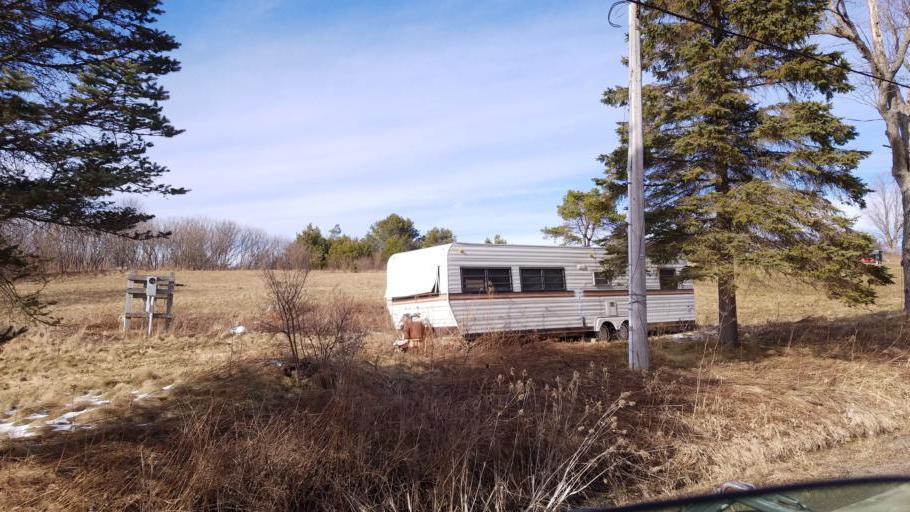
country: US
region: New York
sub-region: Allegany County
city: Wellsville
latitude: 42.0893
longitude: -78.0139
